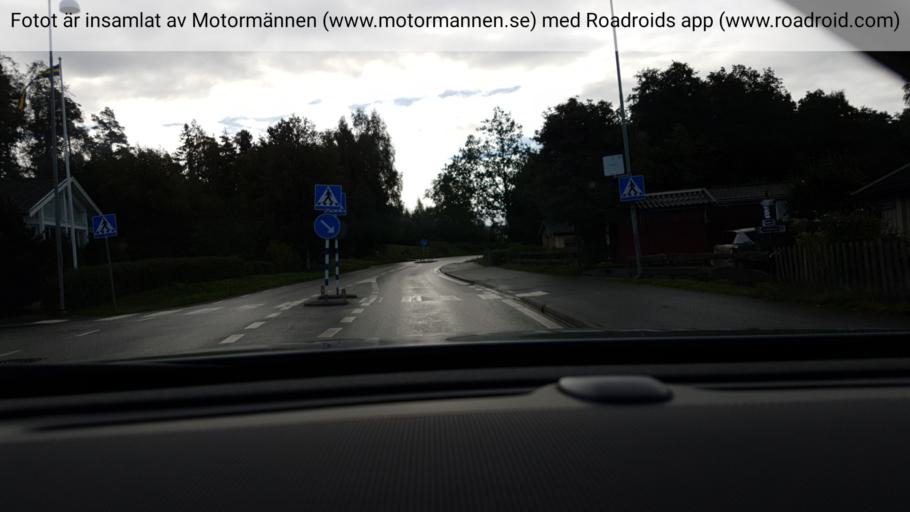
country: SE
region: Vaestra Goetaland
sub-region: Marks Kommun
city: Kinna
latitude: 57.4696
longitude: 12.7126
